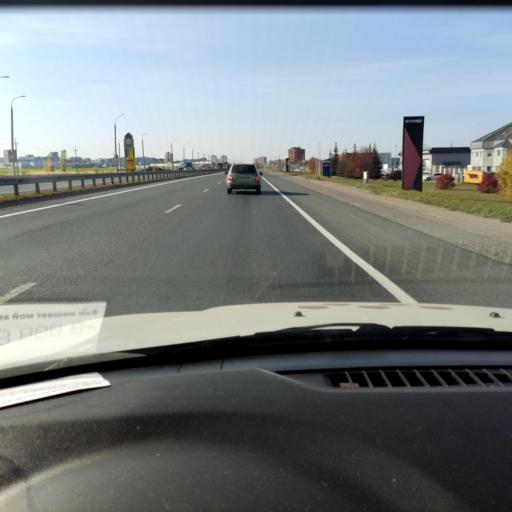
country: RU
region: Samara
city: Tol'yatti
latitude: 53.5592
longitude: 49.3554
